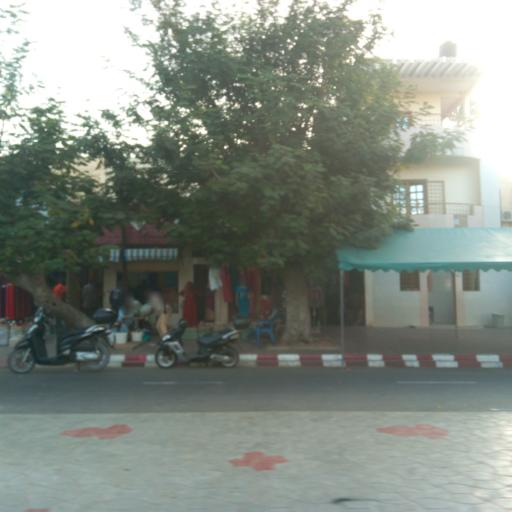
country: SN
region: Dakar
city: Dakar
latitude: 14.6878
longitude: -17.4460
